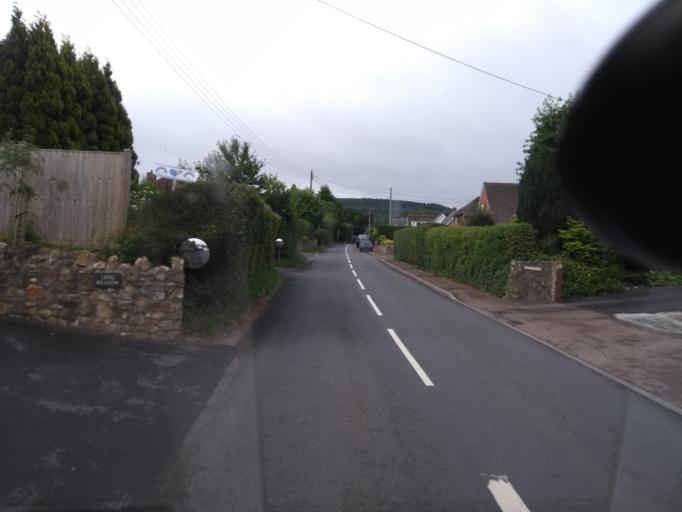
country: GB
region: England
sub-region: Somerset
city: Taunton
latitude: 50.9629
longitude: -3.1240
